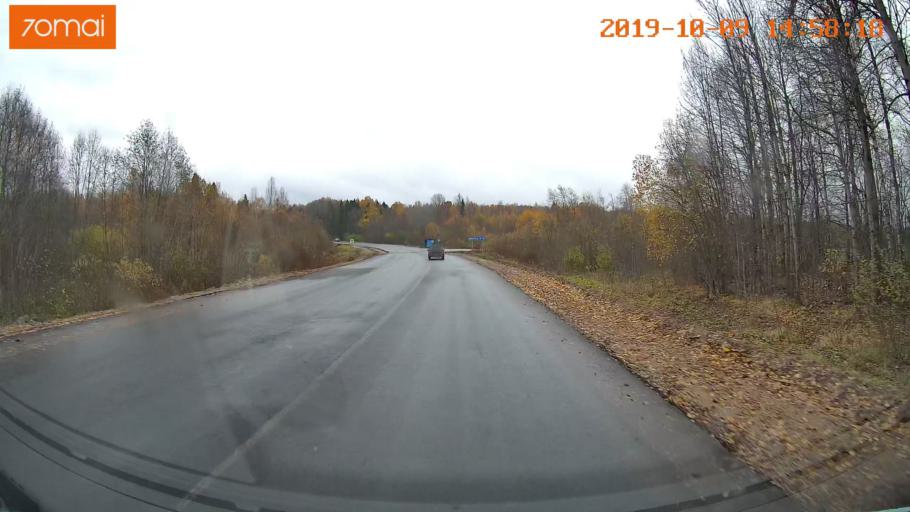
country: RU
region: Kostroma
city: Chistyye Bory
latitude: 58.3282
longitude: 41.6542
